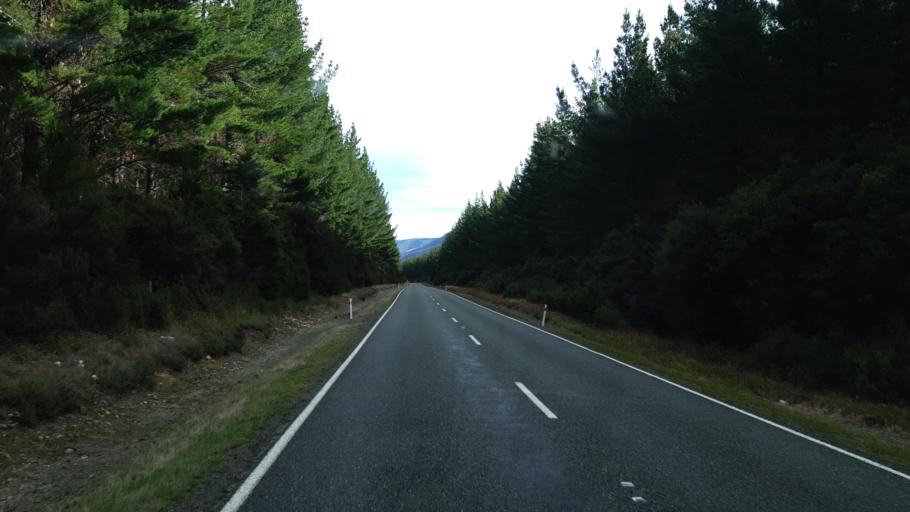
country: NZ
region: Tasman
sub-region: Tasman District
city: Wakefield
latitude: -41.7183
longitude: 173.0716
